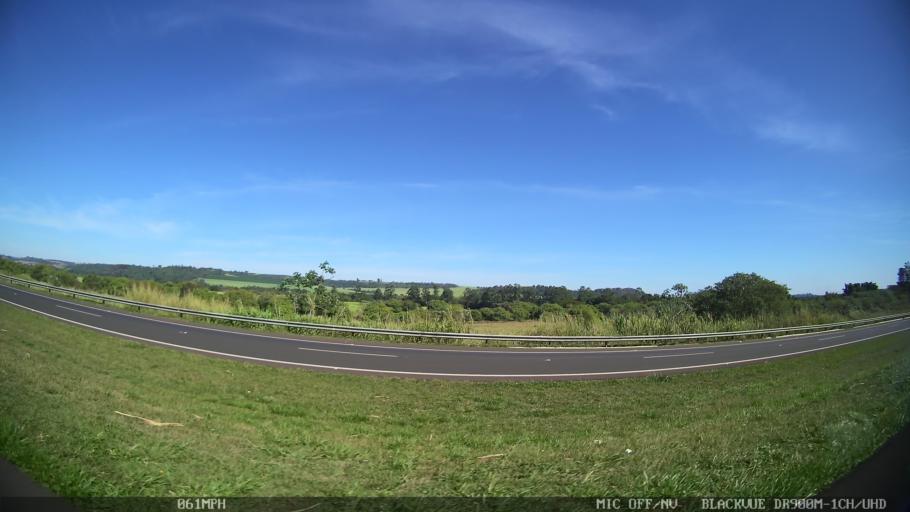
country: BR
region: Sao Paulo
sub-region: Santa Rita Do Passa Quatro
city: Santa Rita do Passa Quatro
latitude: -21.7447
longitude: -47.5762
